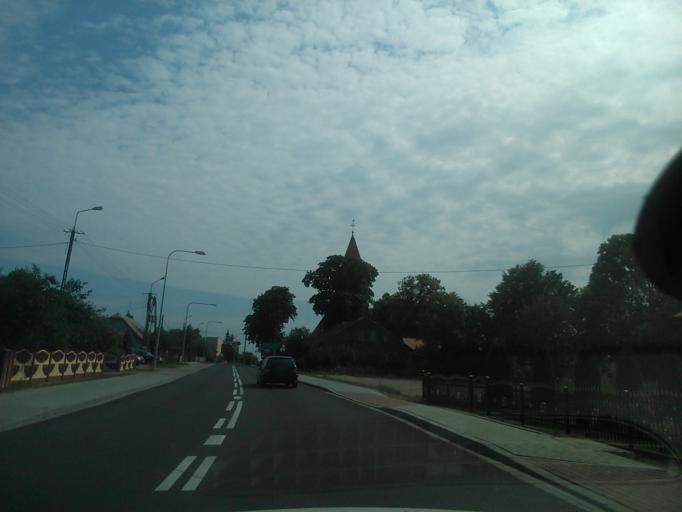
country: PL
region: Warmian-Masurian Voivodeship
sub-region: Powiat dzialdowski
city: Lidzbark
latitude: 53.2349
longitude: 19.9433
